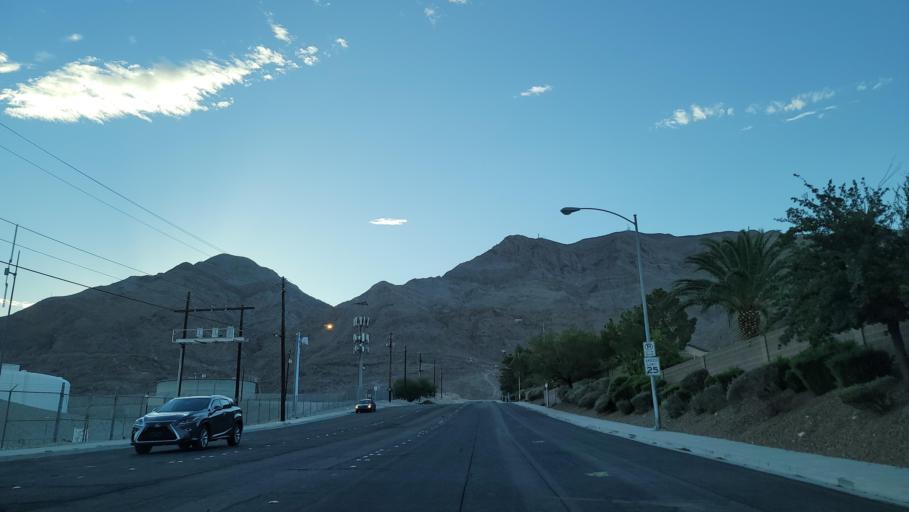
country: US
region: Nevada
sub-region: Clark County
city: Sunrise Manor
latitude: 36.1812
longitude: -115.0202
